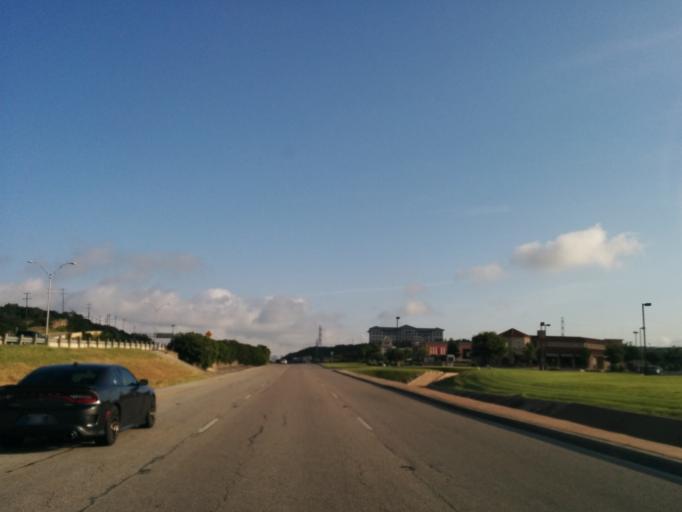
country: US
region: Texas
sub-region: Bexar County
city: Shavano Park
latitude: 29.6094
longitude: -98.6026
